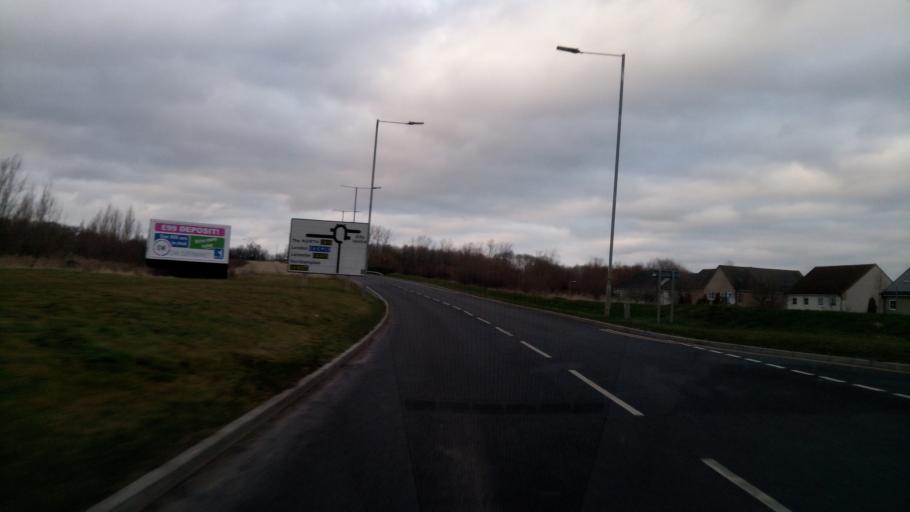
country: GB
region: England
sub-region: Cambridgeshire
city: Yaxley
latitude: 52.5384
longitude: -0.2811
